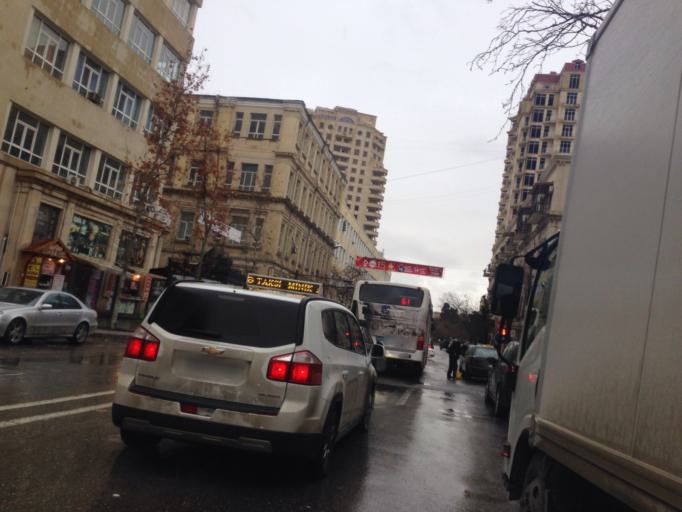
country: AZ
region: Baki
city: Baku
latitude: 40.3775
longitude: 49.8478
